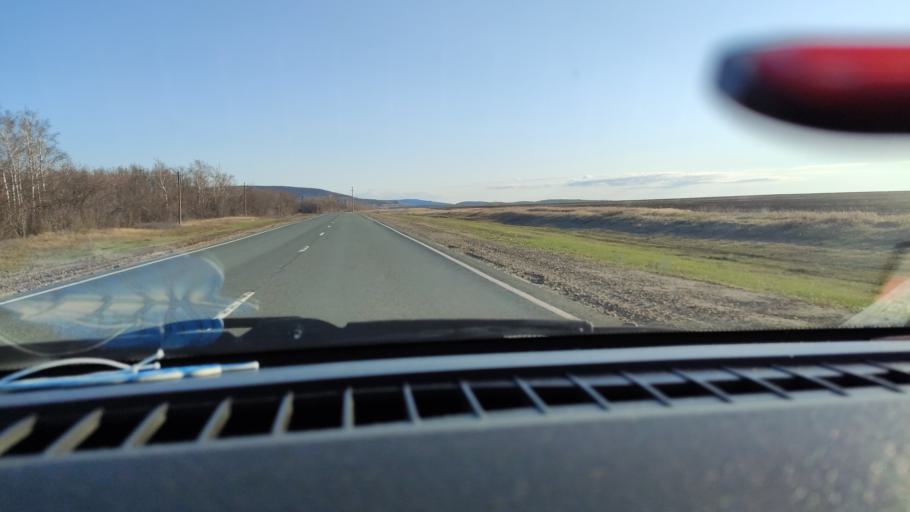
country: RU
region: Saratov
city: Alekseyevka
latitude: 52.2694
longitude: 47.9276
